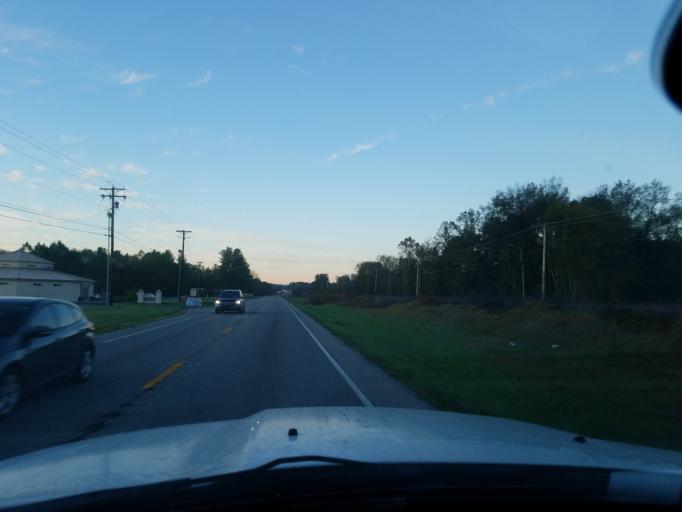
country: US
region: Kentucky
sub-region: Laurel County
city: North Corbin
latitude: 37.0411
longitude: -84.0561
